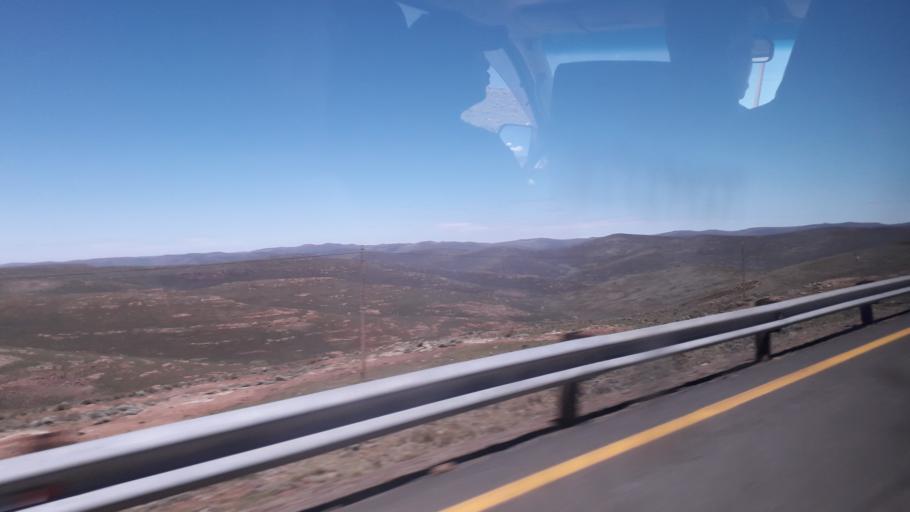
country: LS
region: Mokhotlong
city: Mokhotlong
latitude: -29.0222
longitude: 28.8560
